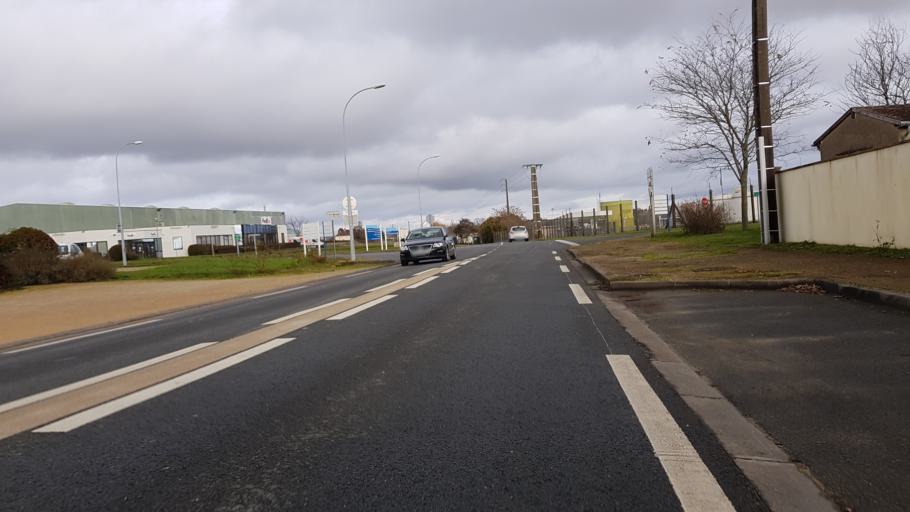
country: FR
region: Poitou-Charentes
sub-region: Departement de la Vienne
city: Chasseneuil-du-Poitou
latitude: 46.6547
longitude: 0.3717
